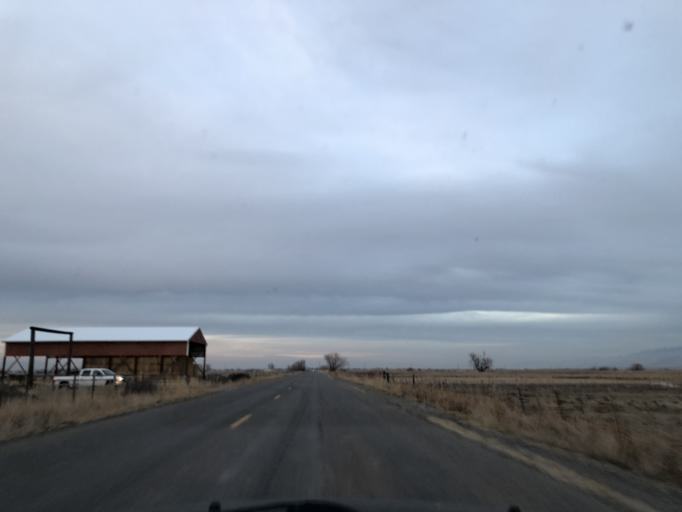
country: US
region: Utah
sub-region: Cache County
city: Benson
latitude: 41.7531
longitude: -111.9116
